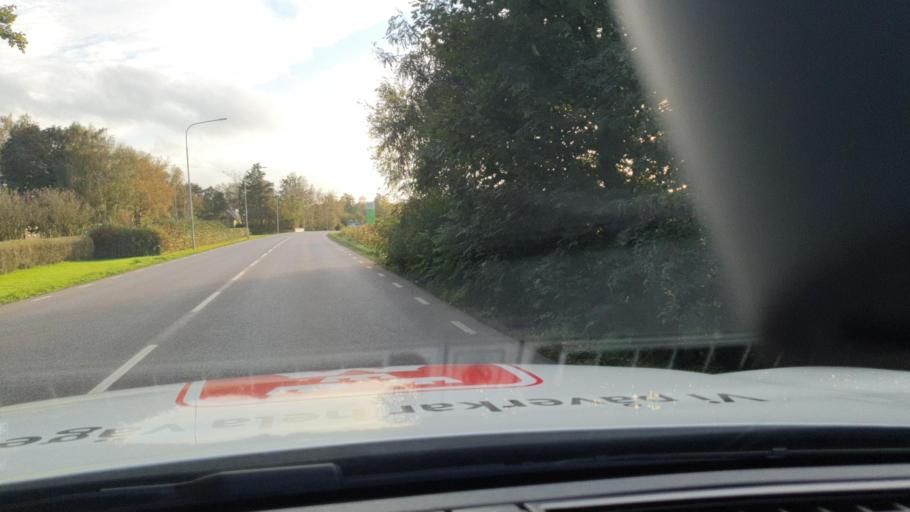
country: SE
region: Halland
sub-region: Laholms Kommun
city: Laholm
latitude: 56.4717
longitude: 13.0318
